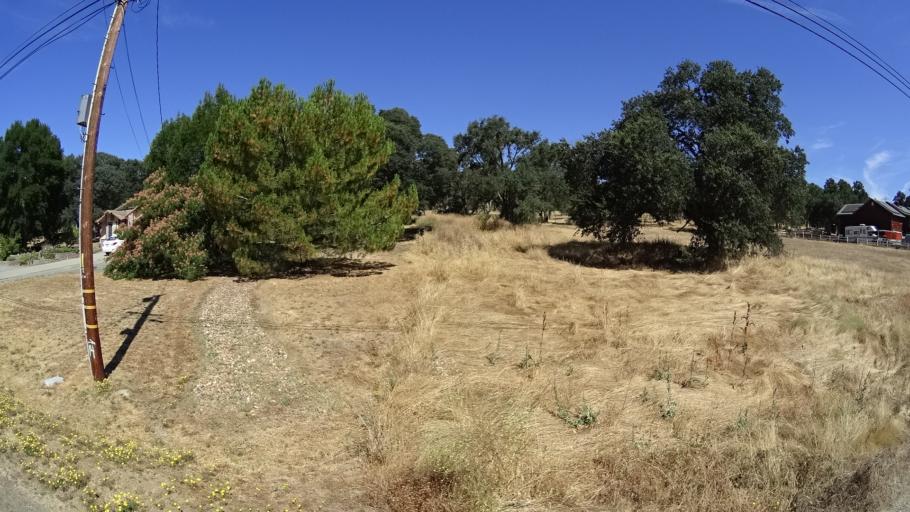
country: US
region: California
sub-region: Calaveras County
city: Rancho Calaveras
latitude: 38.1462
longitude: -120.8639
